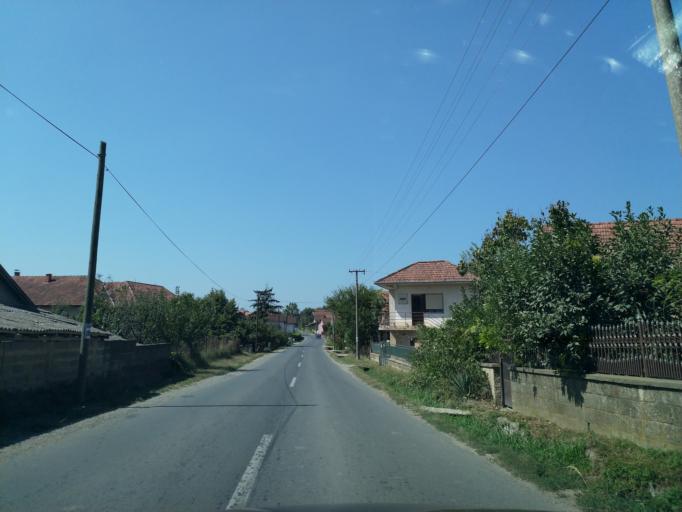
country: RS
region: Central Serbia
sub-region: Rasinski Okrug
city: Krusevac
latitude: 43.6139
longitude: 21.2044
